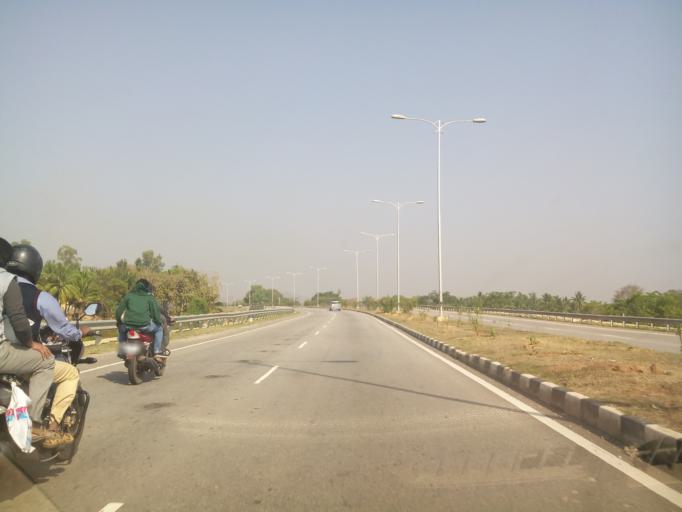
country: IN
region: Karnataka
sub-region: Tumkur
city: Kunigal
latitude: 13.0033
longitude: 77.0164
